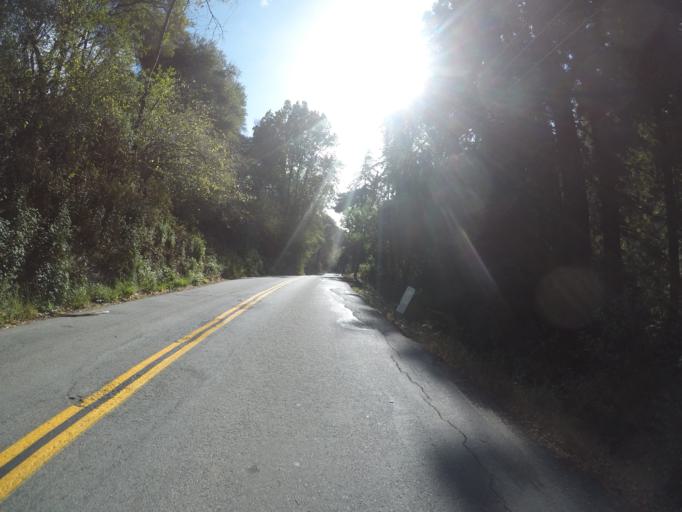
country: US
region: California
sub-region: Santa Cruz County
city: Live Oak
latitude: 36.9964
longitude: -121.9707
